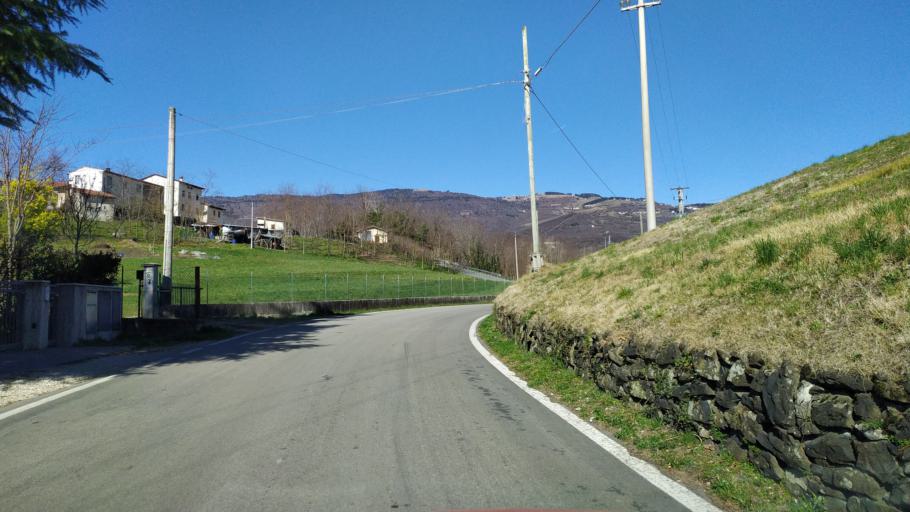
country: IT
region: Veneto
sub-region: Provincia di Vicenza
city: Fara Vicentino
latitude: 45.7501
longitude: 11.5431
